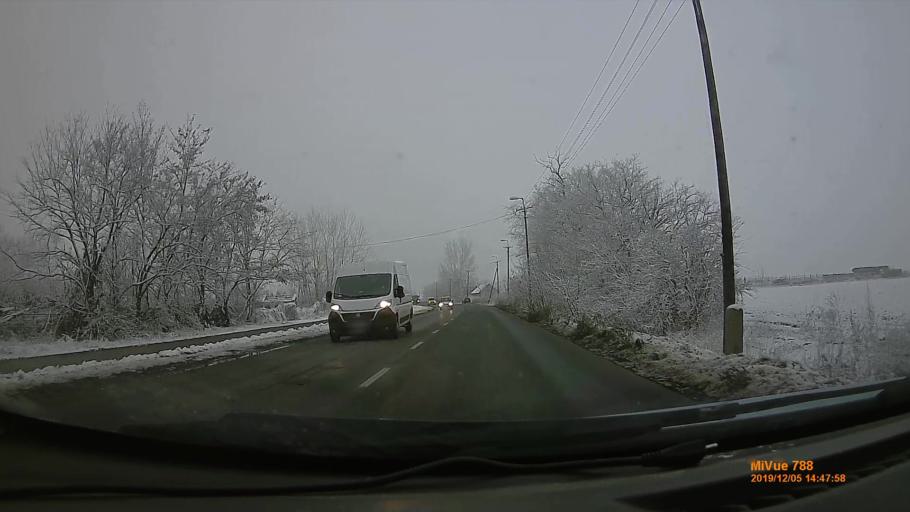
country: HU
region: Szabolcs-Szatmar-Bereg
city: Nyiregyhaza
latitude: 47.9729
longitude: 21.6917
